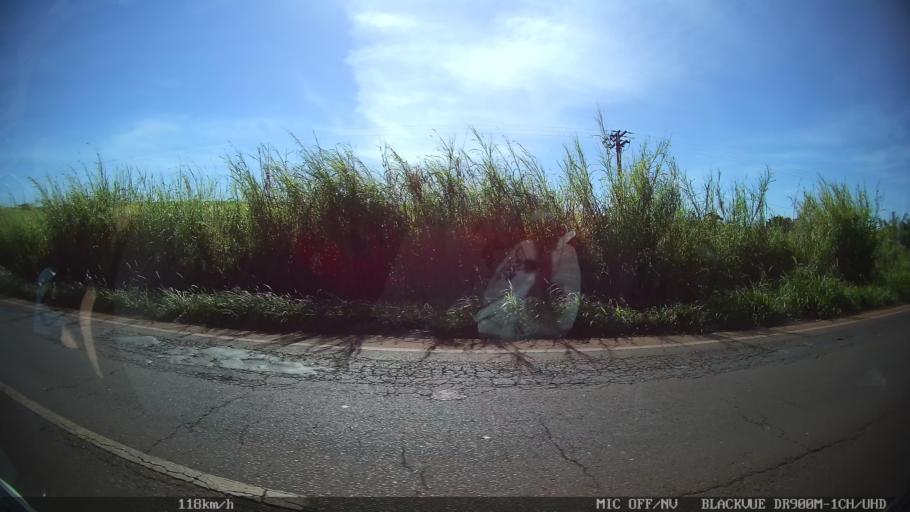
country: BR
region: Sao Paulo
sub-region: Ipua
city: Ipua
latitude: -20.4929
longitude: -48.0183
